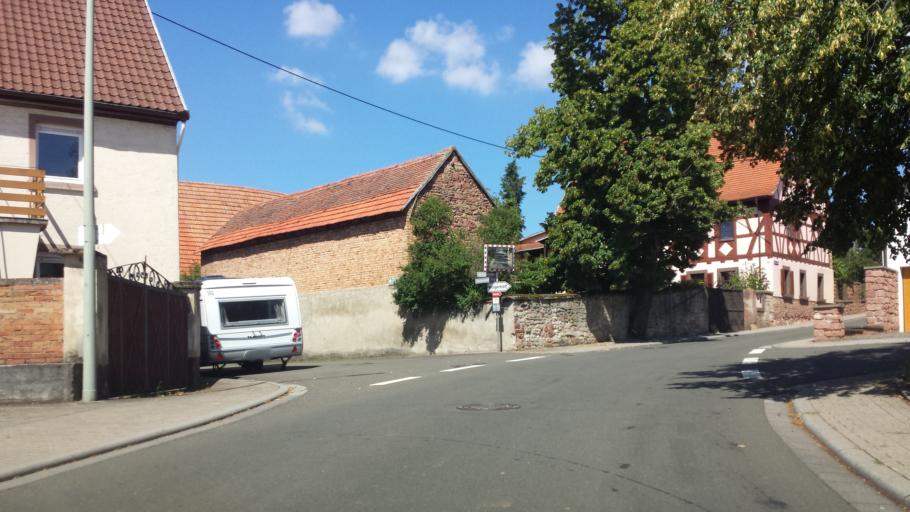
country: DE
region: Rheinland-Pfalz
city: Weitersweiler
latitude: 49.6151
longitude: 7.9958
